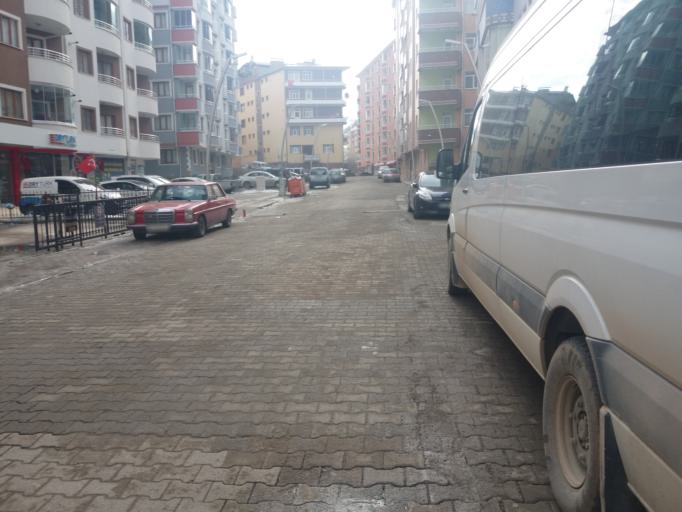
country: TR
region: Gumushane
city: Gumushkhane
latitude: 40.4562
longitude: 39.4889
